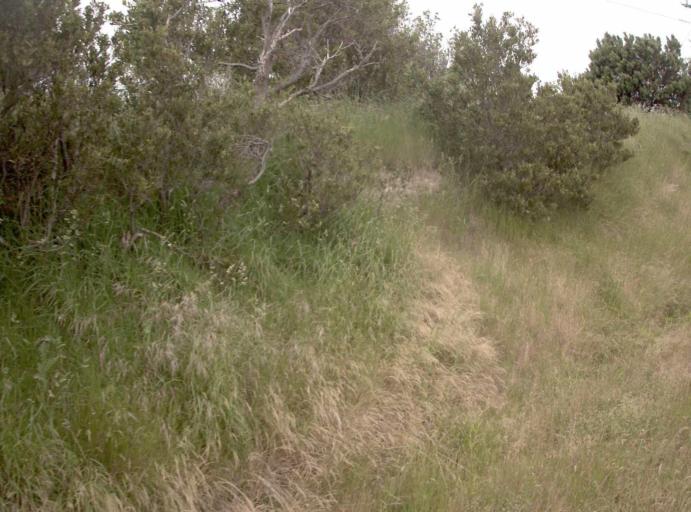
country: AU
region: Victoria
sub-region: Bass Coast
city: North Wonthaggi
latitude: -38.4587
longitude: 145.7910
